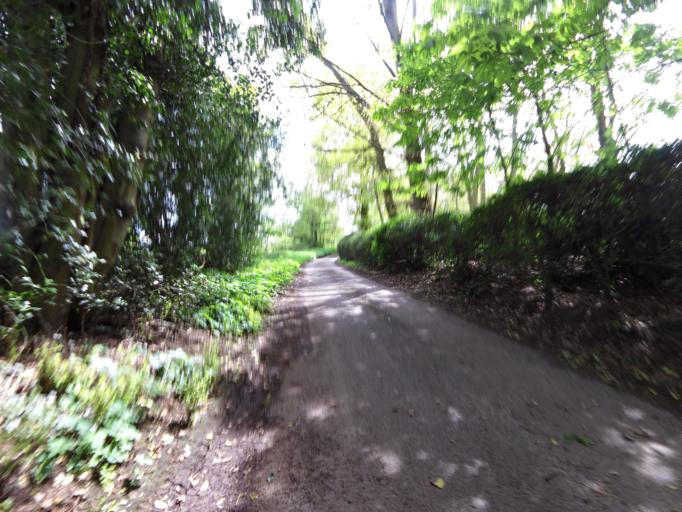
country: GB
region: England
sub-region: Suffolk
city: Ipswich
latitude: 51.9942
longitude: 1.1474
